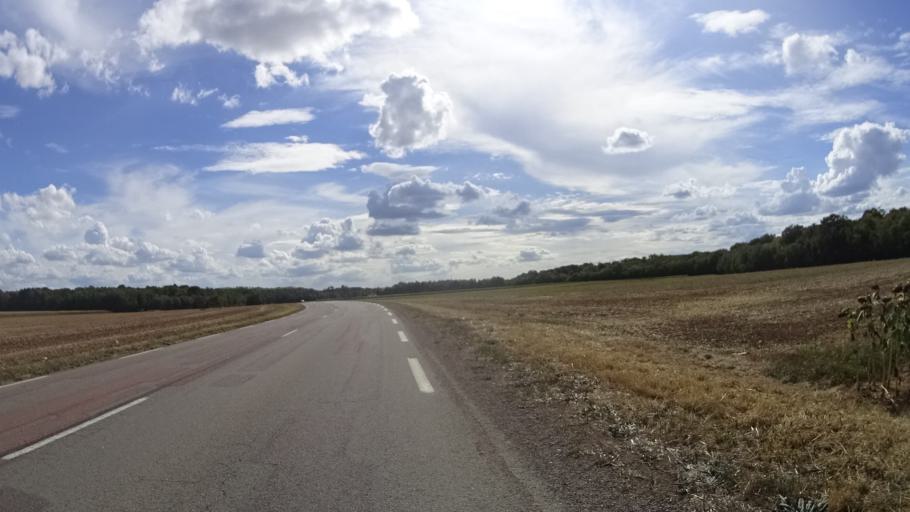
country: FR
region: Bourgogne
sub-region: Departement de la Cote-d'Or
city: Seurre
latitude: 47.0422
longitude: 5.1888
